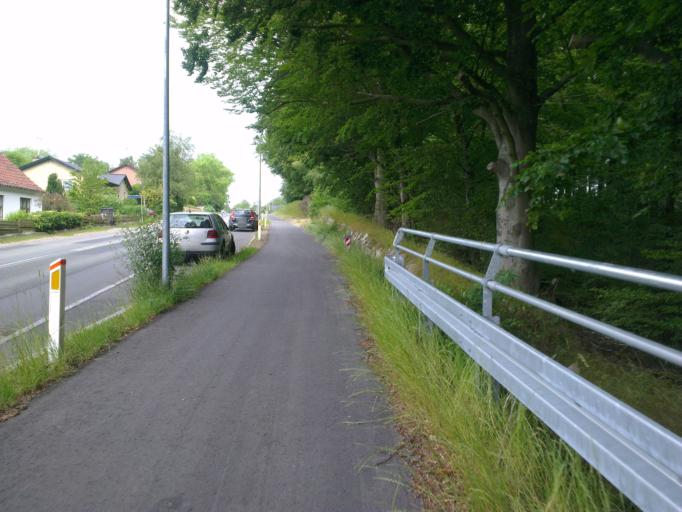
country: DK
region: Capital Region
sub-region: Allerod Kommune
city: Lillerod
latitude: 55.9044
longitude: 12.3411
